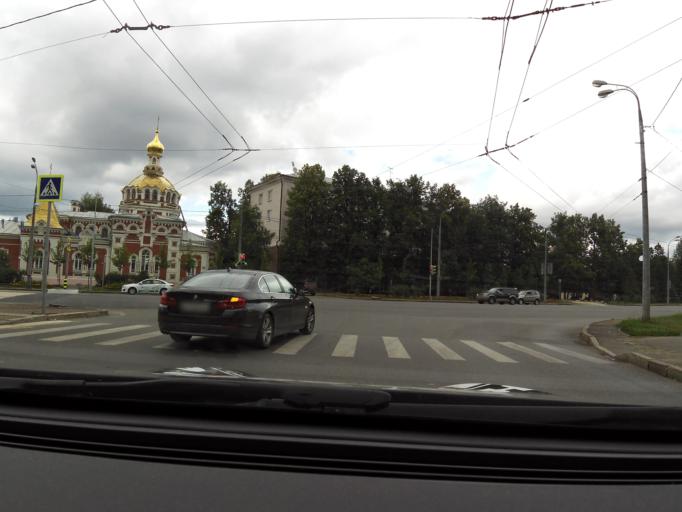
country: RU
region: Tatarstan
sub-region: Gorod Kazan'
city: Kazan
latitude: 55.7938
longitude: 49.1434
